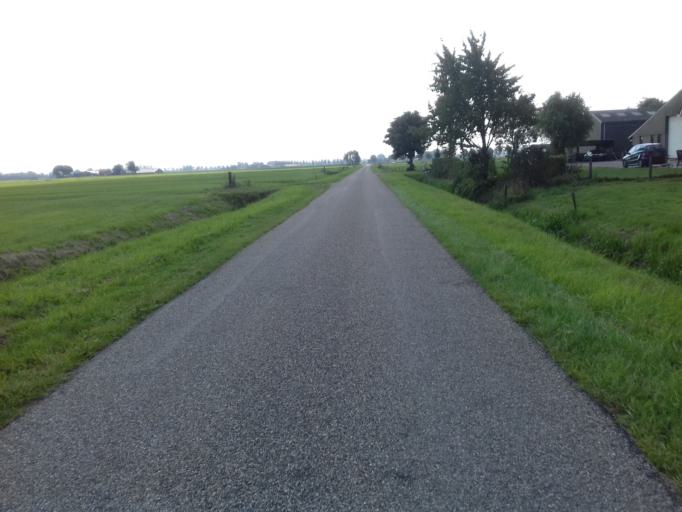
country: NL
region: Gelderland
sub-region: Gemeente Zaltbommel
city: Zaltbommel
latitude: 51.8661
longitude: 5.1851
